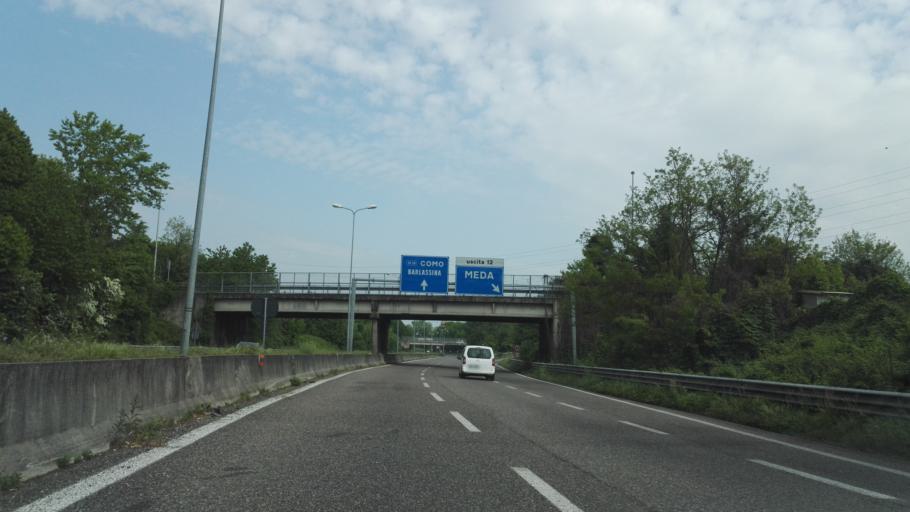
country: IT
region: Lombardy
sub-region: Provincia di Monza e Brianza
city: Seveso
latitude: 45.6499
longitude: 9.1540
